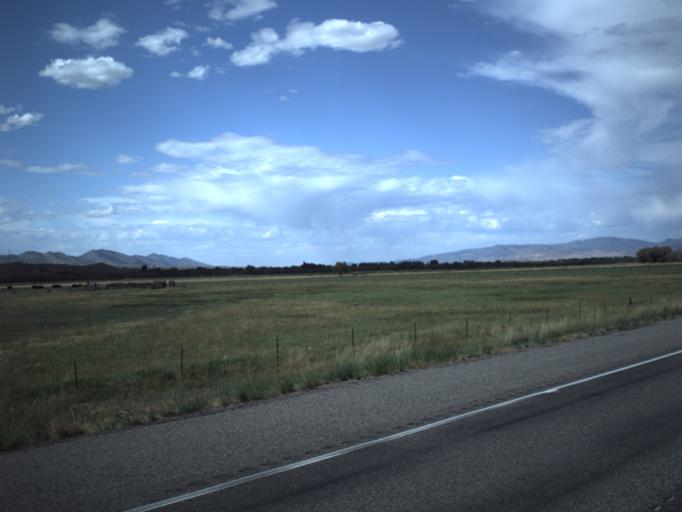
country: US
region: Utah
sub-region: Sevier County
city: Salina
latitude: 38.9759
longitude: -111.8575
